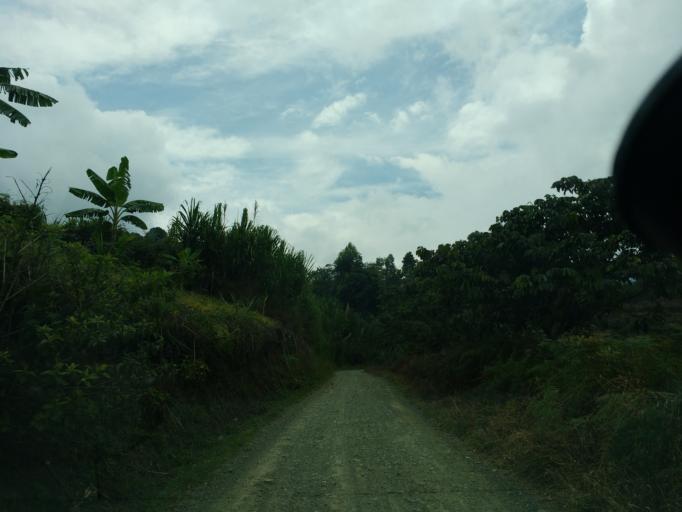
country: CO
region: Cauca
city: Santander de Quilichao
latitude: 2.9154
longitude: -76.4780
